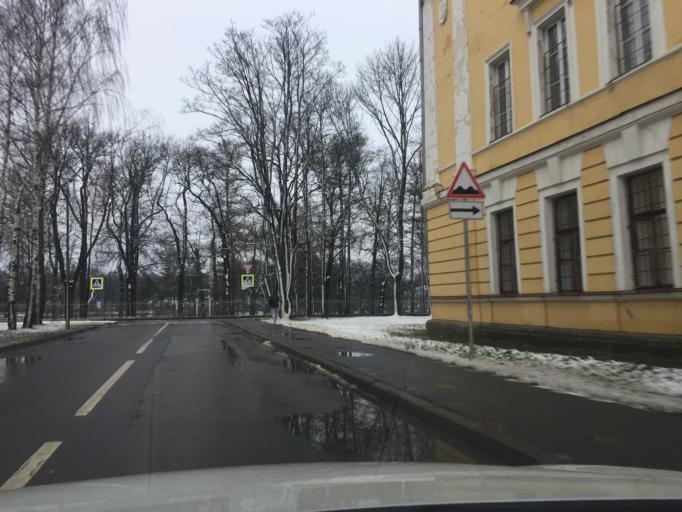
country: RU
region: St.-Petersburg
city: Pushkin
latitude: 59.7082
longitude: 30.3943
